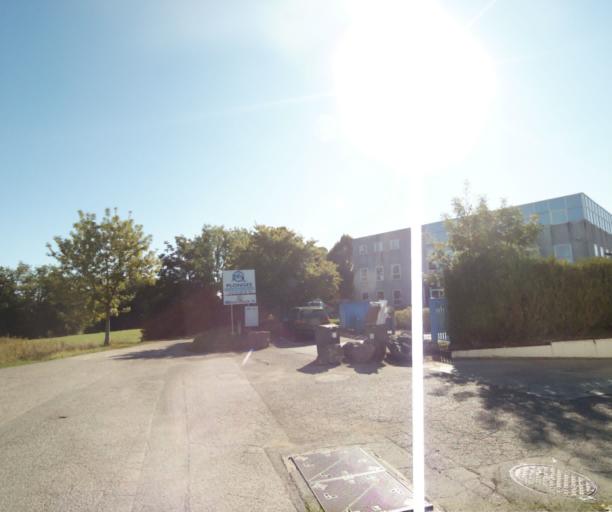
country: FR
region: Rhone-Alpes
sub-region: Departement de l'Ain
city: Ferney-Voltaire
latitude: 46.2519
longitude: 6.1225
